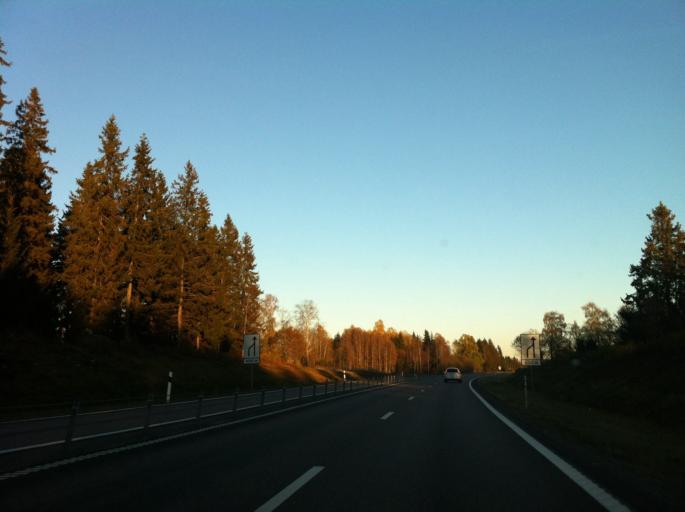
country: SE
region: Gaevleborg
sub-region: Sandvikens Kommun
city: Jarbo
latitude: 60.6104
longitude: 16.6152
